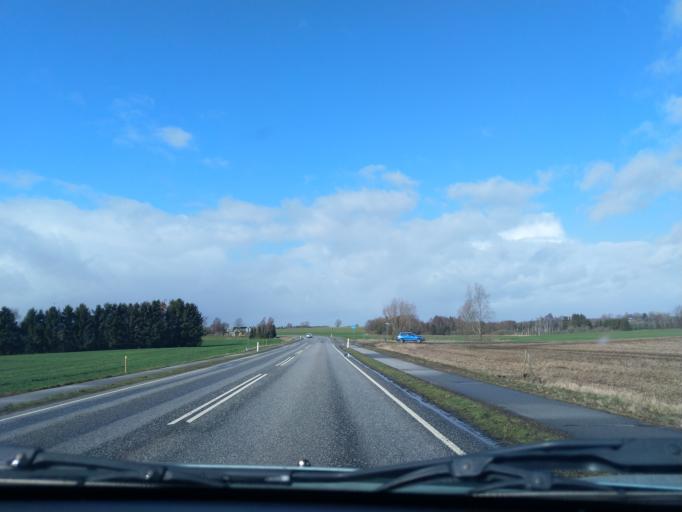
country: DK
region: Zealand
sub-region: Naestved Kommune
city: Naestved
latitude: 55.2901
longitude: 11.7041
